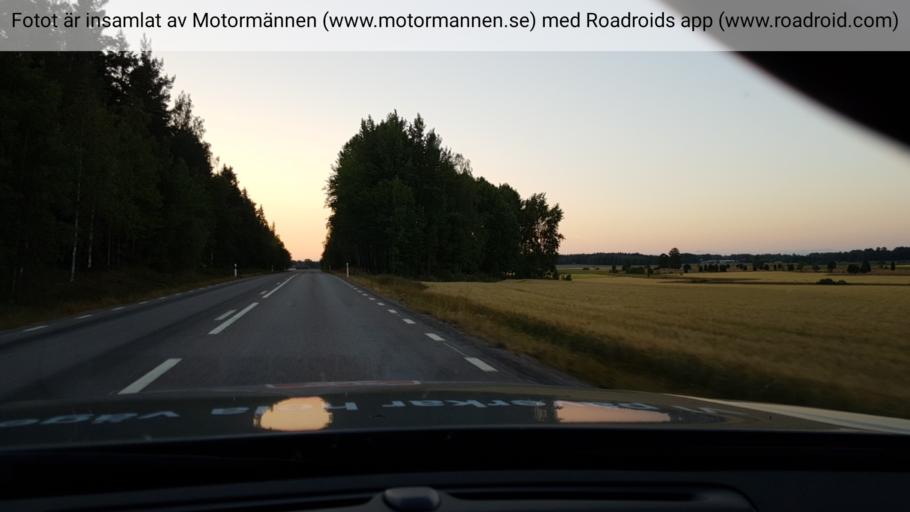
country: SE
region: Uppsala
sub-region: Heby Kommun
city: OEstervala
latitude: 60.0845
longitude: 17.1912
